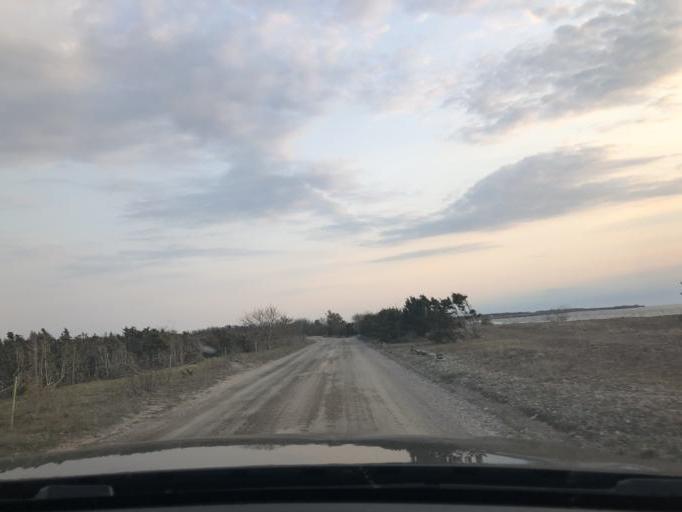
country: SE
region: Kalmar
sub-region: Borgholms Kommun
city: Borgholm
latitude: 57.2183
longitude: 16.9482
